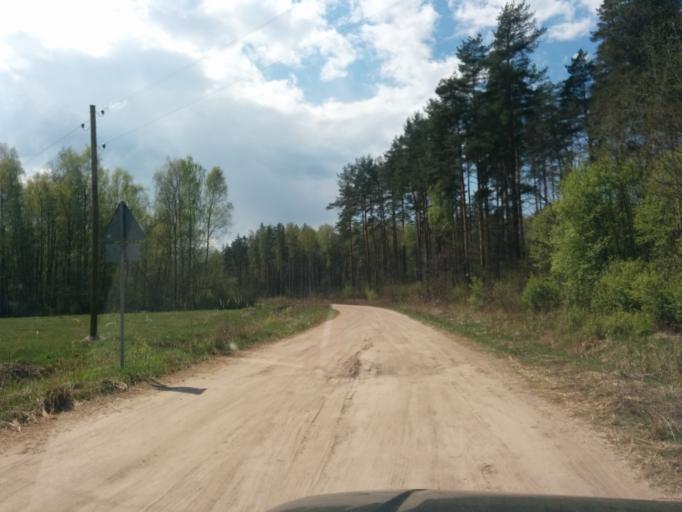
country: LV
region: Ozolnieku
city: Ozolnieki
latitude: 56.6128
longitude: 23.7848
